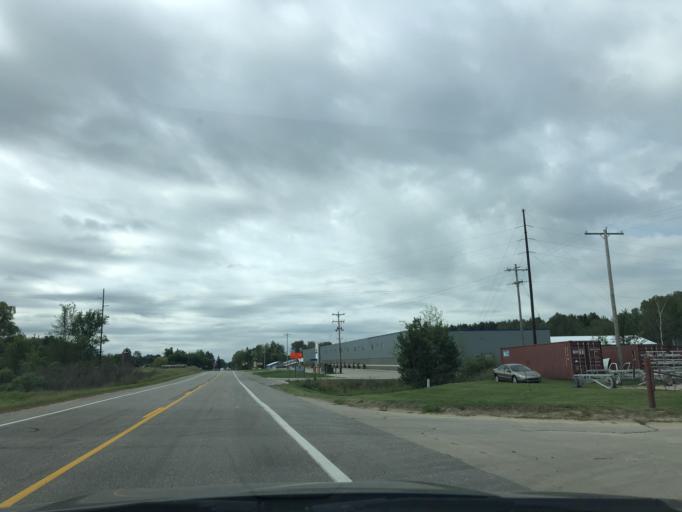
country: US
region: Michigan
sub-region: Missaukee County
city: Lake City
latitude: 44.1147
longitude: -85.1476
